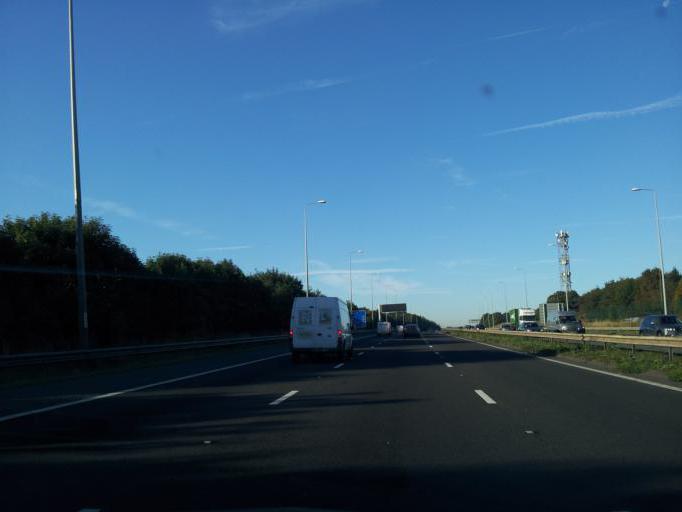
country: GB
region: England
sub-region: Calderdale
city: Elland
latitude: 53.6642
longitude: -1.8486
